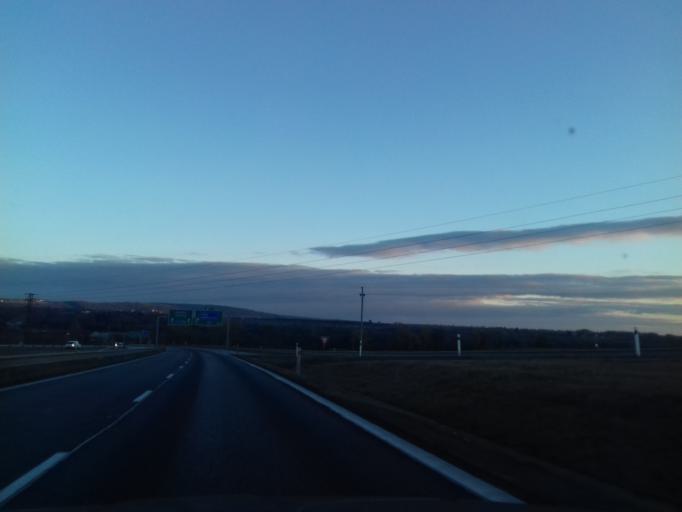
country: CZ
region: South Moravian
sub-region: Okres Vyskov
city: Vyskov
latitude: 49.2736
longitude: 17.0208
